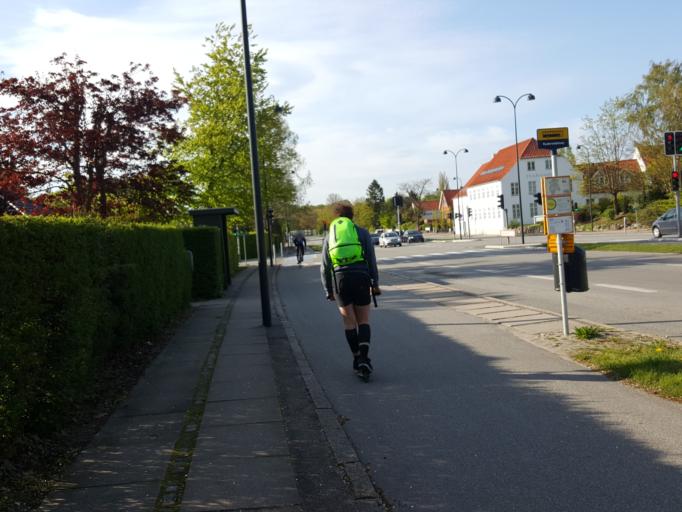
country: DK
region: Capital Region
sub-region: Rudersdal Kommune
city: Holte
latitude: 55.8196
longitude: 12.4667
